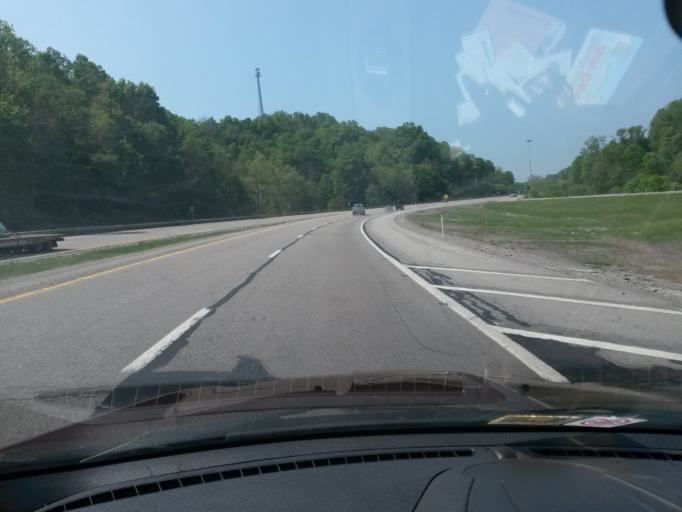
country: US
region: West Virginia
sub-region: Lewis County
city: Weston
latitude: 38.9626
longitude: -80.5161
